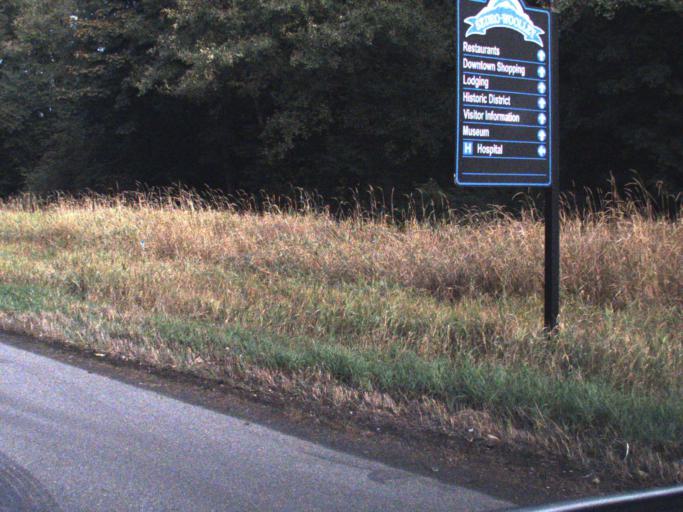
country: US
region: Washington
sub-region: Skagit County
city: Sedro-Woolley
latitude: 48.4936
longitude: -122.2775
